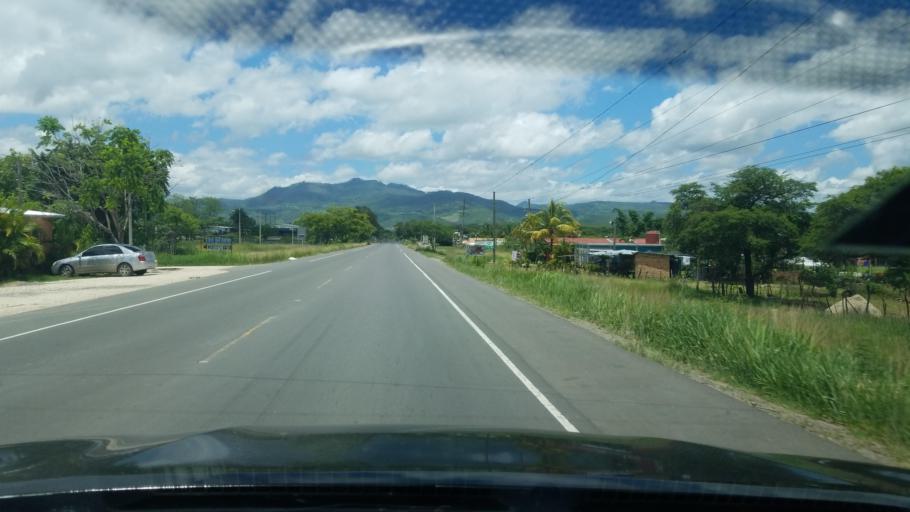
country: HN
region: Francisco Morazan
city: Cofradia
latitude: 14.2910
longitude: -87.2427
